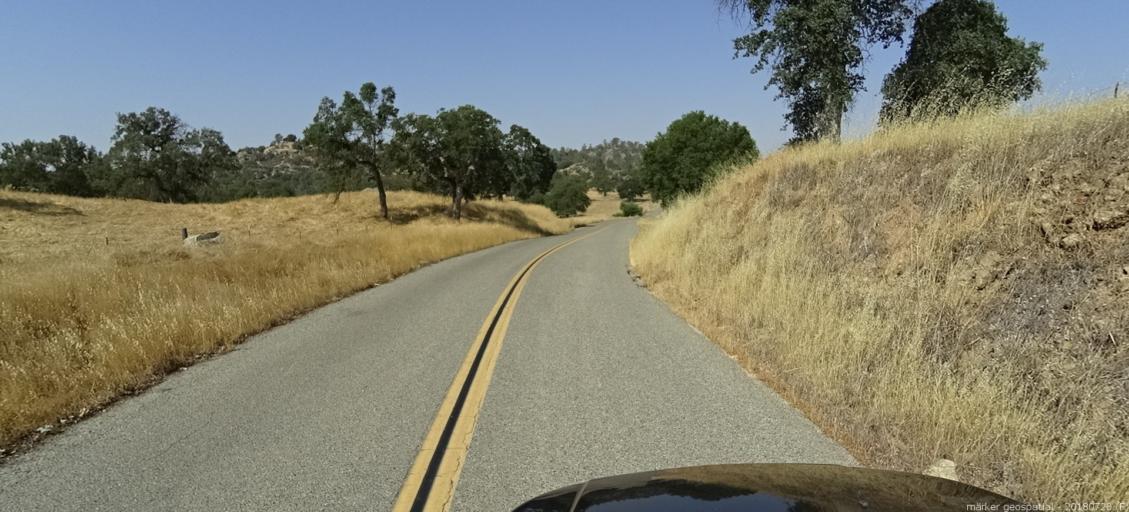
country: US
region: California
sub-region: Madera County
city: Yosemite Lakes
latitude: 37.2589
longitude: -119.9483
